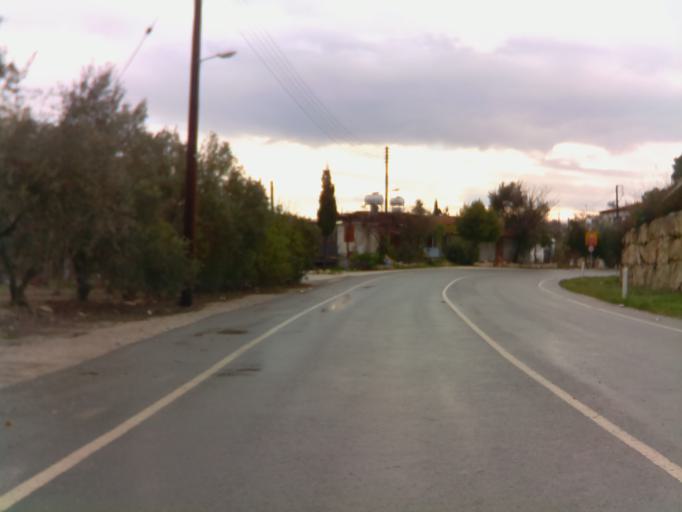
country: CY
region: Pafos
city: Tala
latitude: 34.8914
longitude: 32.4761
